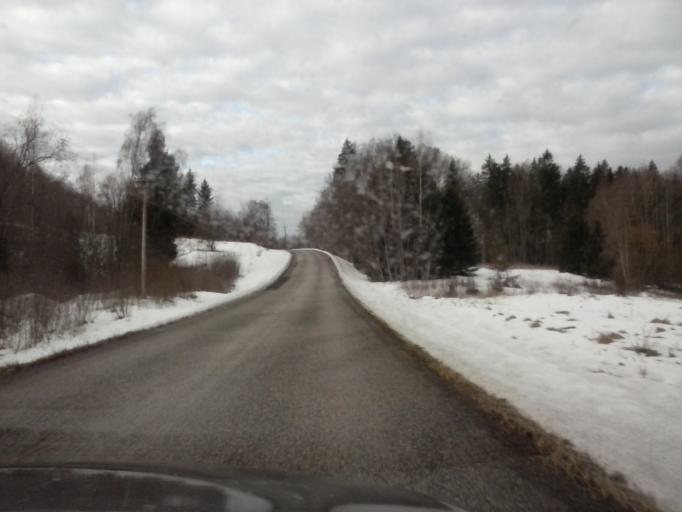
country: EE
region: Tartu
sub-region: Elva linn
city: Elva
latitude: 58.0103
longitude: 26.2971
